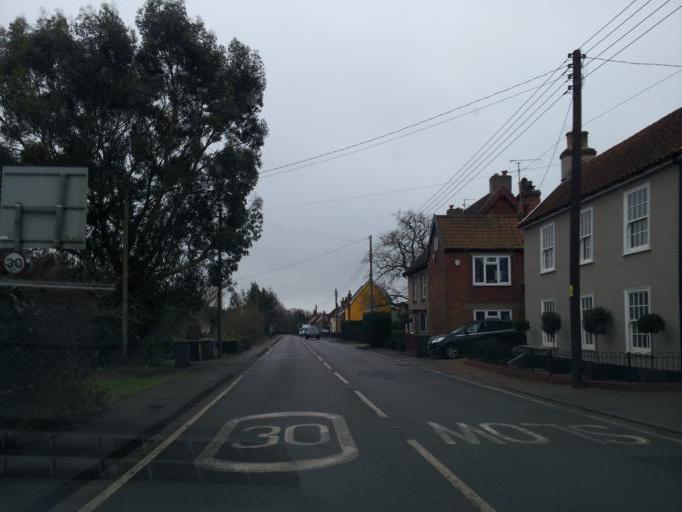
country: GB
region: England
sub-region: Essex
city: Mistley
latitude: 51.9885
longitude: 1.0974
